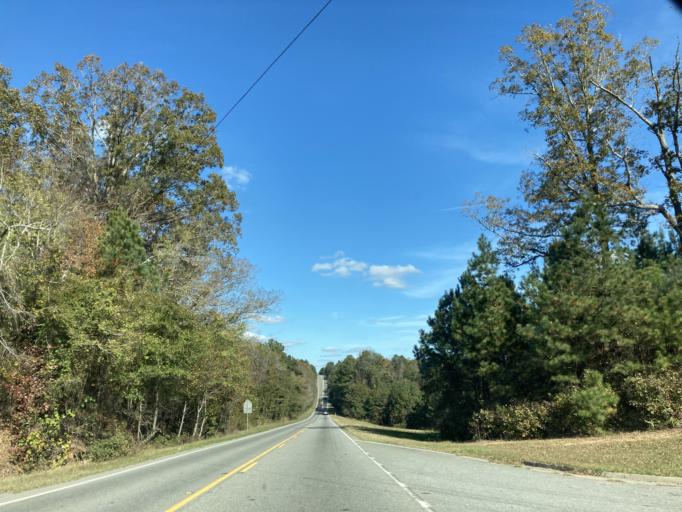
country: US
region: Georgia
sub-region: Bibb County
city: Macon
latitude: 32.8944
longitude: -83.5317
